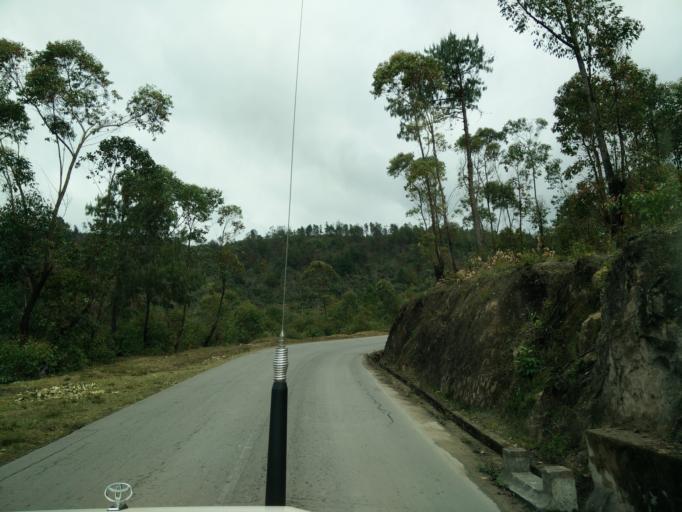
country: MG
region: Upper Matsiatra
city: Fianarantsoa
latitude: -21.2649
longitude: 47.2373
